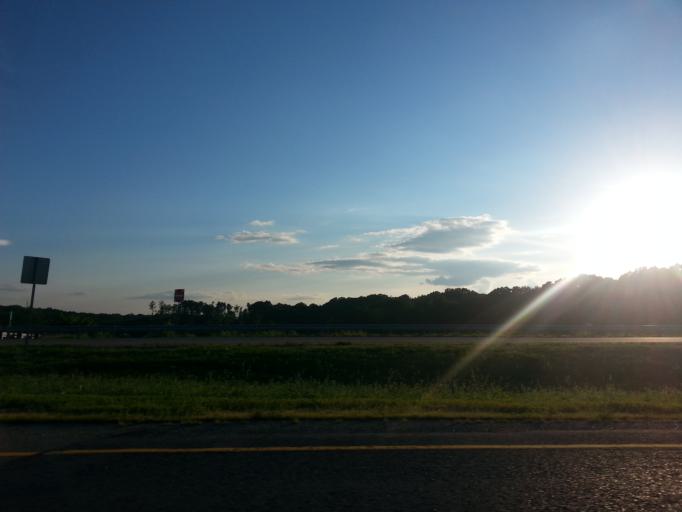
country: US
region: Tennessee
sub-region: Loudon County
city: Lenoir City
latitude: 35.7507
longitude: -84.2155
